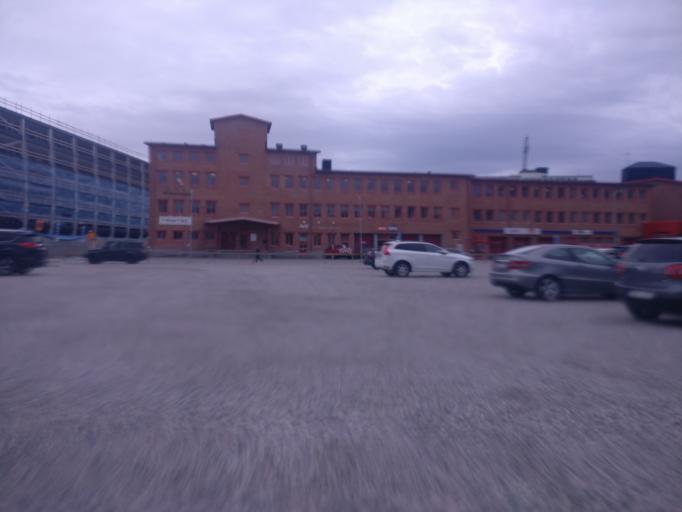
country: SE
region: Vaesternorrland
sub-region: Sundsvalls Kommun
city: Sundsvall
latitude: 62.3890
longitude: 17.3170
